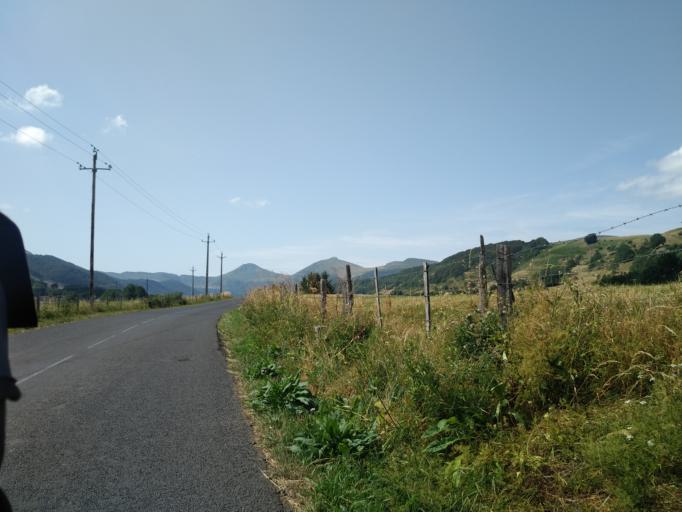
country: FR
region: Auvergne
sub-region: Departement du Cantal
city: Riom-es-Montagnes
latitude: 45.1716
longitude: 2.7148
